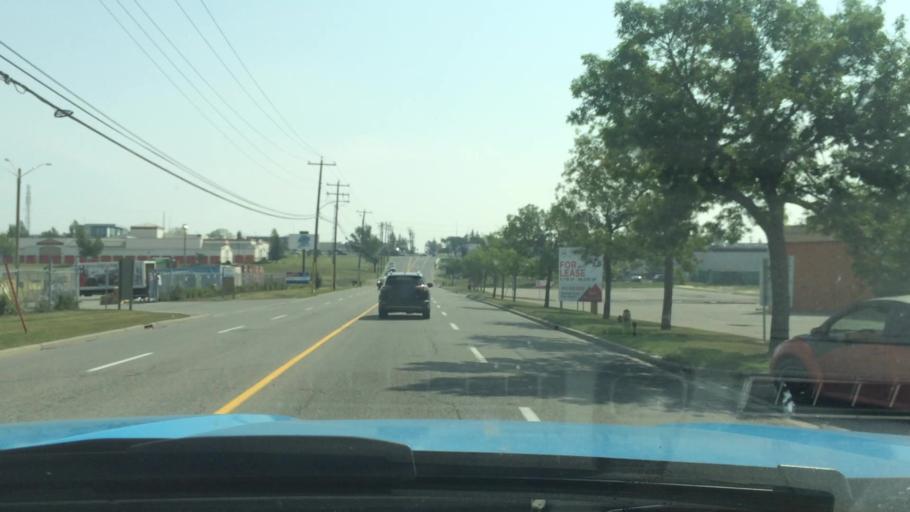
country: CA
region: Alberta
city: Calgary
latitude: 51.0524
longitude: -114.0070
